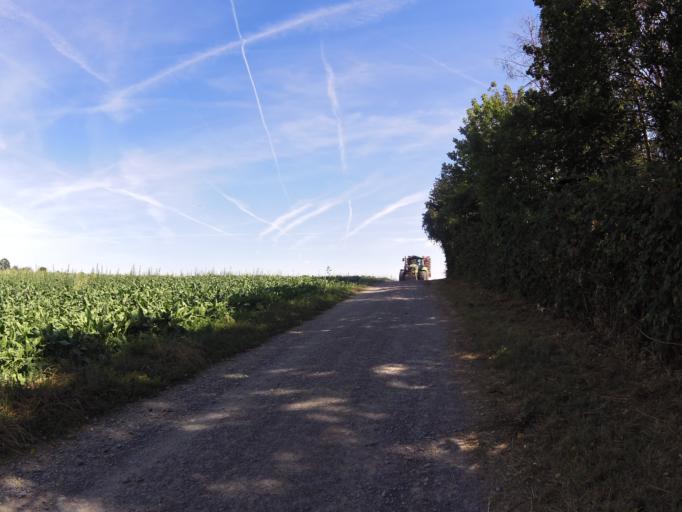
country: DE
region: Bavaria
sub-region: Regierungsbezirk Unterfranken
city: Hettstadt
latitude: 49.8067
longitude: 9.8339
